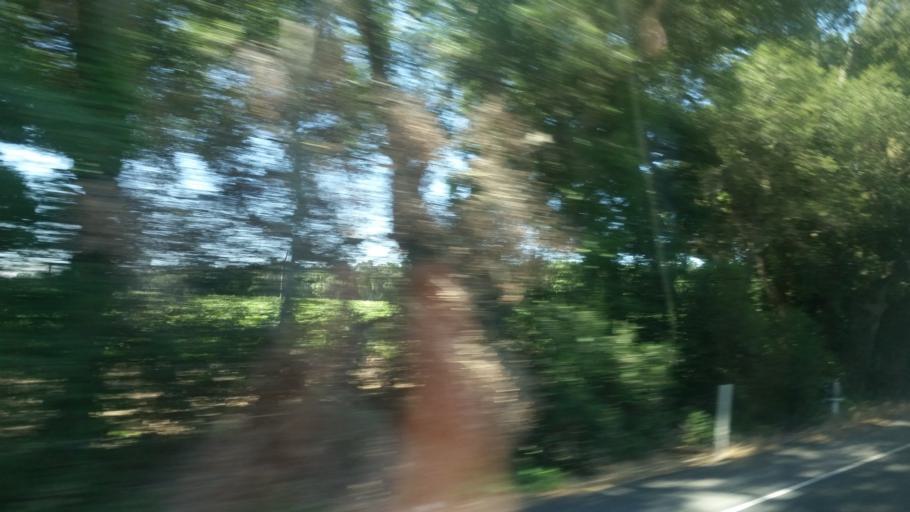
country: US
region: California
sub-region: Sonoma County
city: Temelec
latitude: 38.2773
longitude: -122.4743
